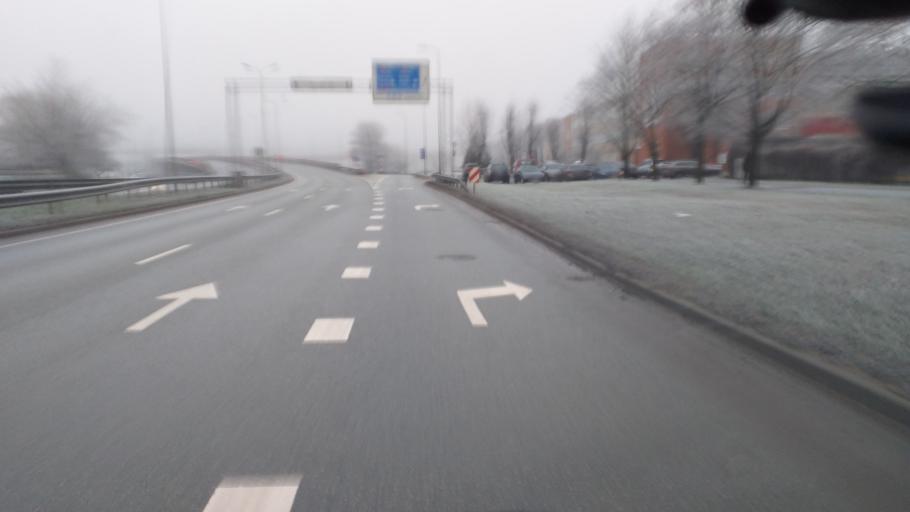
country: LV
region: Riga
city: Riga
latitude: 56.9277
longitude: 24.1862
